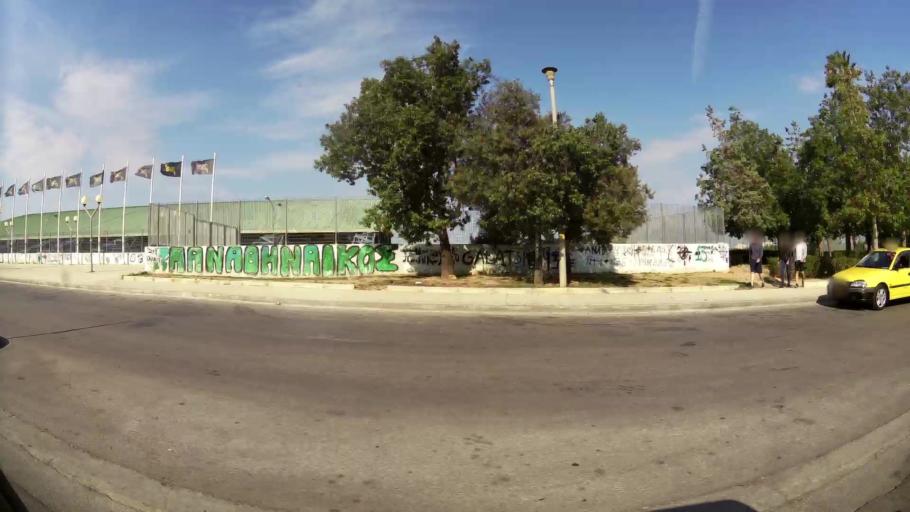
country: GR
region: Attica
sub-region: Nomarchia Athinas
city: Nea Ionia
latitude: 38.0272
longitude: 23.7621
